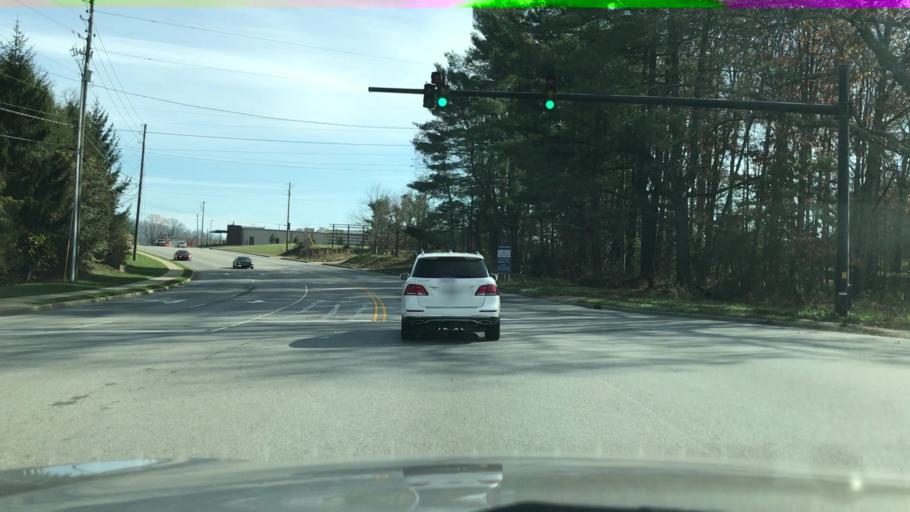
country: US
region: North Carolina
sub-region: Buncombe County
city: Royal Pines
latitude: 35.4800
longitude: -82.5481
